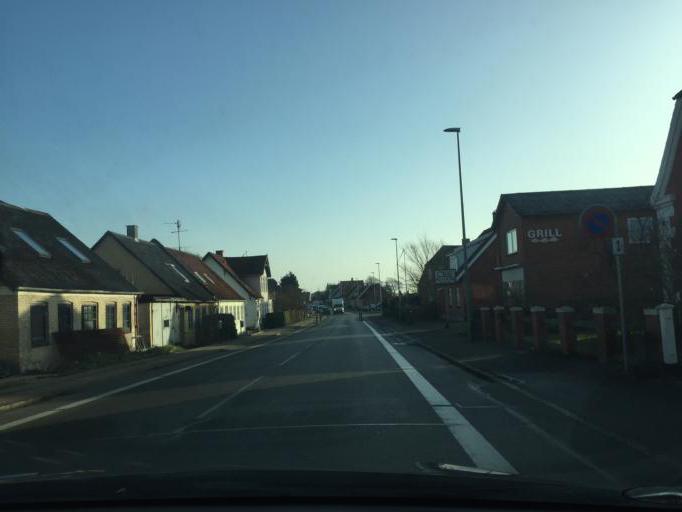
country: DK
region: South Denmark
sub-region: Faaborg-Midtfyn Kommune
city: Faaborg
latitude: 55.1029
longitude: 10.2277
